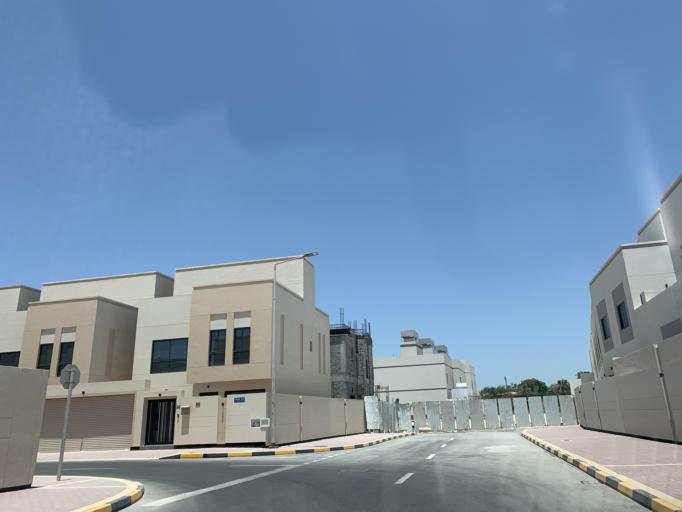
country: BH
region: Manama
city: Jidd Hafs
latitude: 26.2335
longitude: 50.4972
